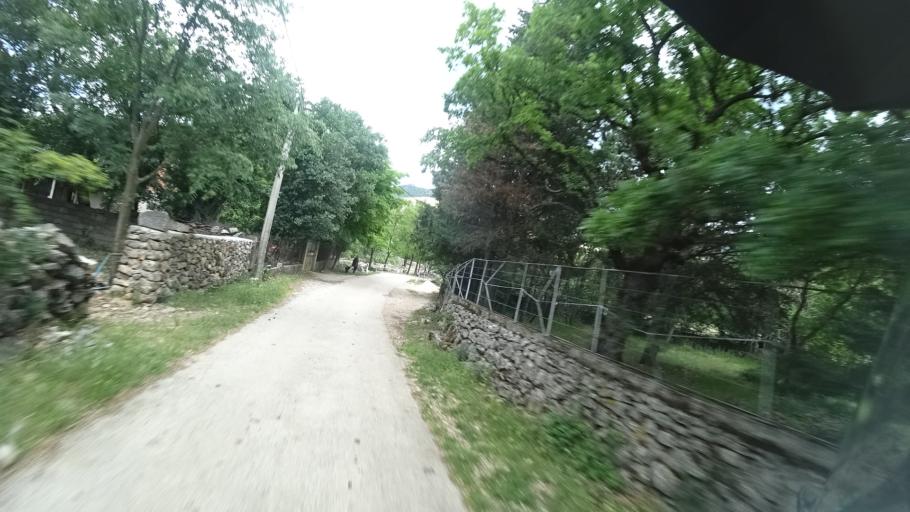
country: HR
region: Zadarska
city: Gracac
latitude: 44.1916
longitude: 15.9080
